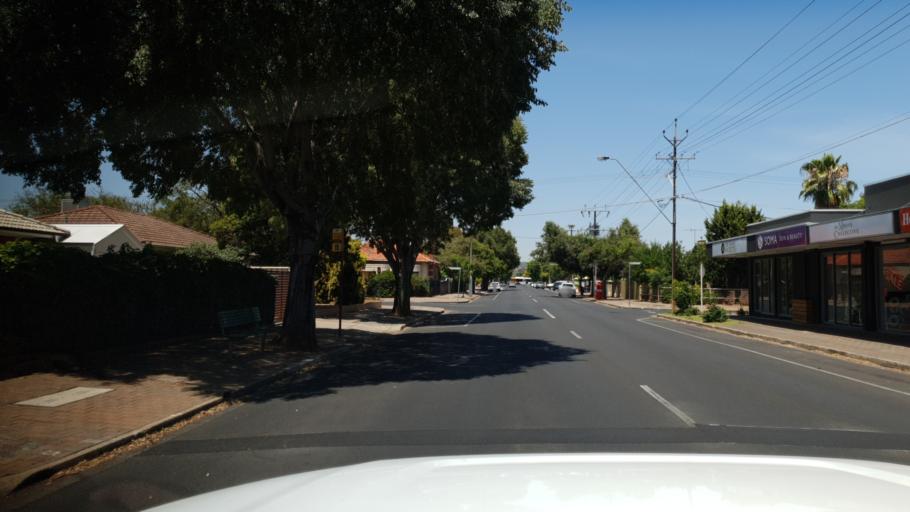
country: AU
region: South Australia
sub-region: Mitcham
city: Clarence Gardens
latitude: -34.9748
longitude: 138.5824
